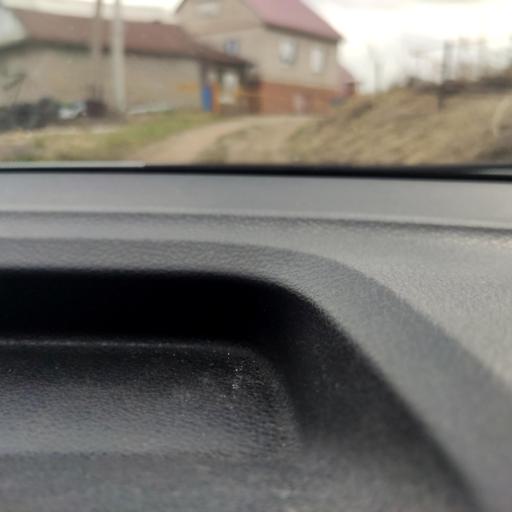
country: RU
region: Bashkortostan
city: Blagoveshchensk
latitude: 54.9134
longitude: 56.1088
